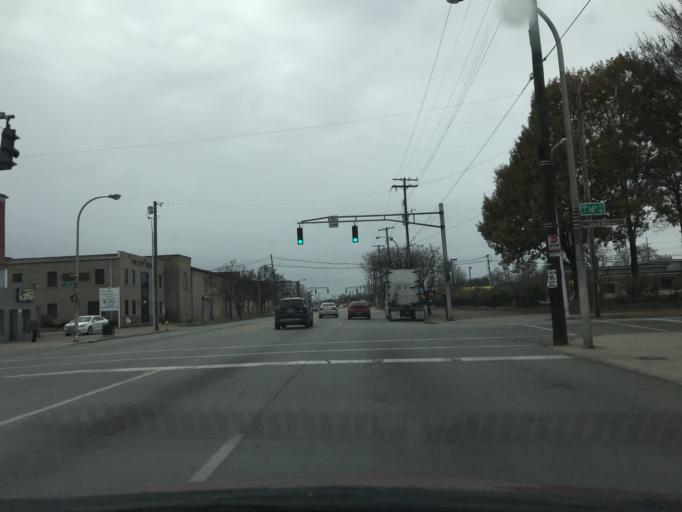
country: US
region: Kentucky
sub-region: Jefferson County
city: Louisville
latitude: 38.2485
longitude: -85.7779
